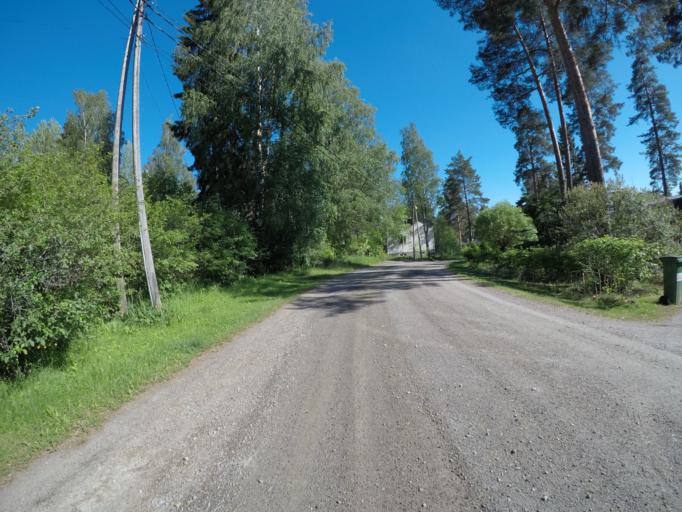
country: FI
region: Haeme
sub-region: Haemeenlinna
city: Haemeenlinna
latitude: 61.0115
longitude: 24.4838
